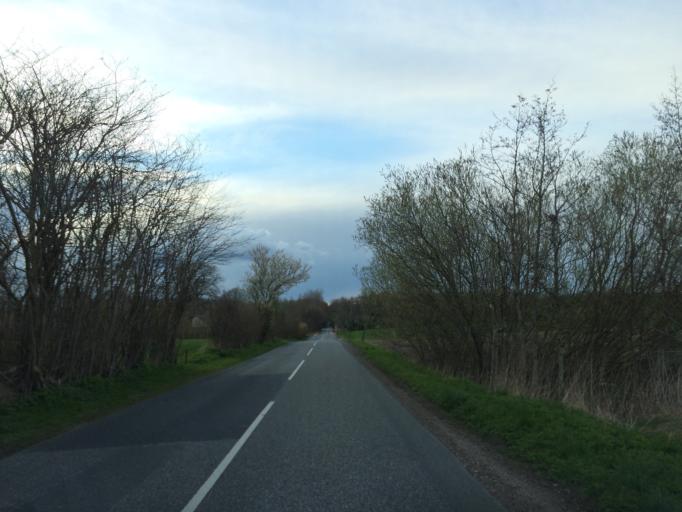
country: DK
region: South Denmark
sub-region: Odense Kommune
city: Bellinge
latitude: 55.2841
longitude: 10.2966
